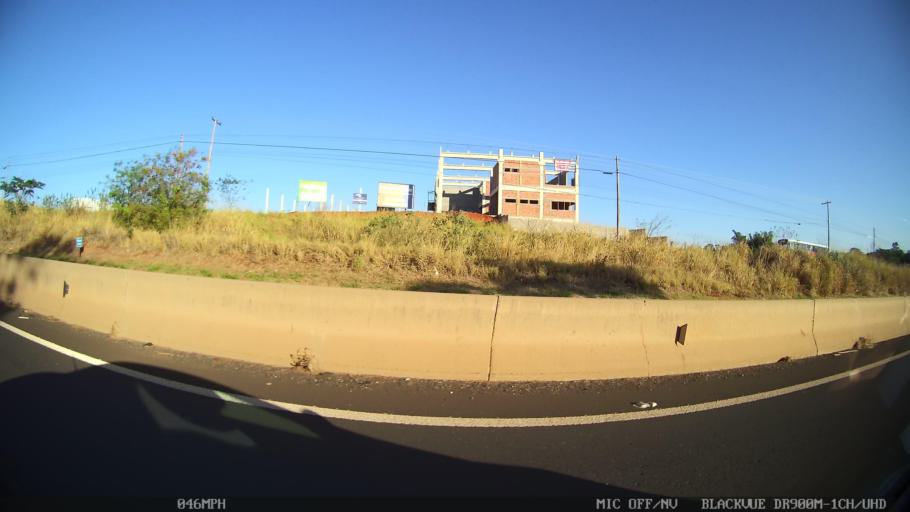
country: BR
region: Sao Paulo
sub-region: Guapiacu
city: Guapiacu
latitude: -20.7834
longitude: -49.2679
